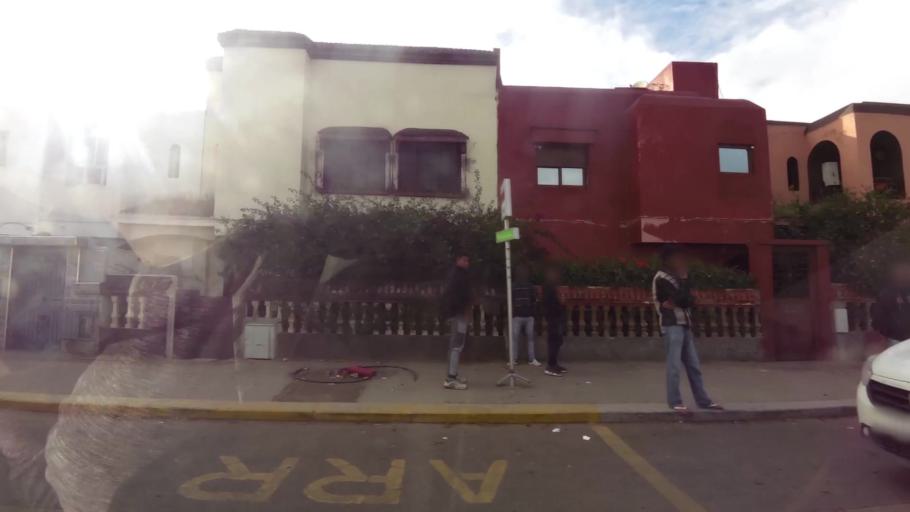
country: MA
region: Doukkala-Abda
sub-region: El-Jadida
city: El Jadida
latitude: 33.2474
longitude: -8.5181
